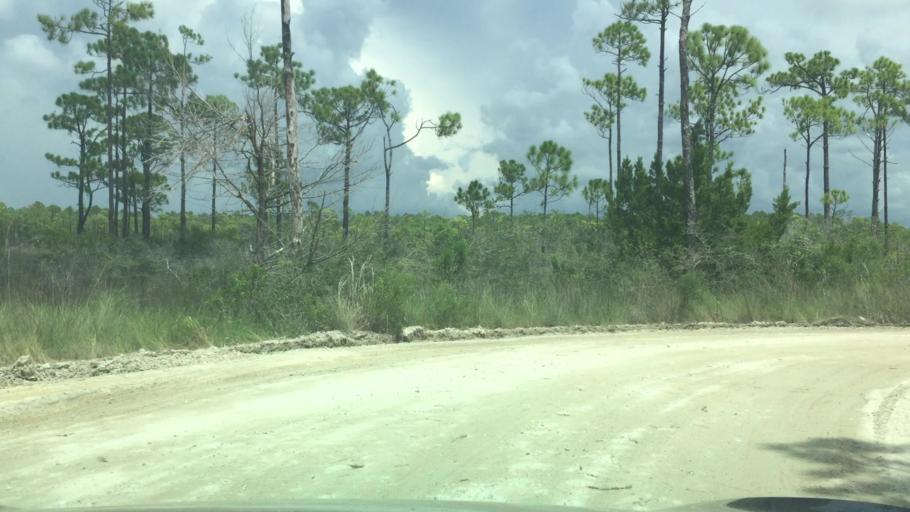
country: US
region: Florida
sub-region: Bay County
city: Mexico Beach
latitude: 29.9612
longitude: -85.4566
